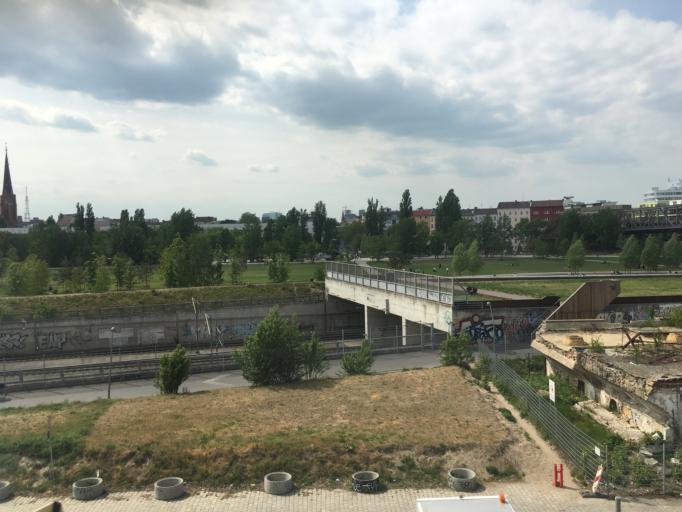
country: DE
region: Berlin
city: Tiergarten Bezirk
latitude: 52.4981
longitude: 13.3737
